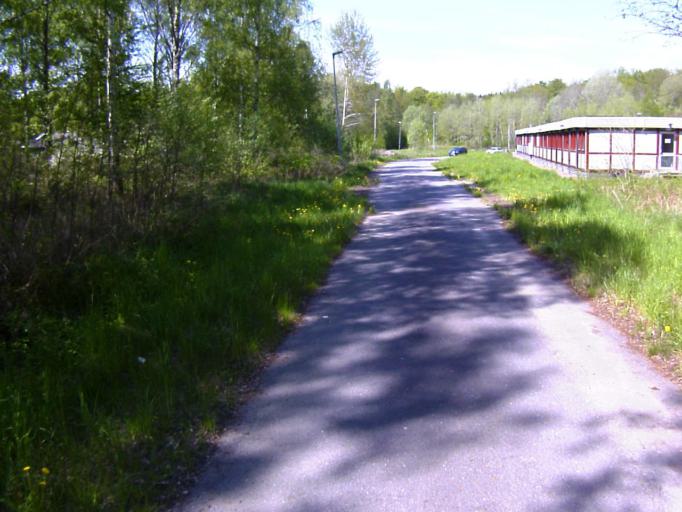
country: SE
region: Skane
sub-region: Kristianstads Kommun
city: Tollarp
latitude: 56.1724
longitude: 14.2999
